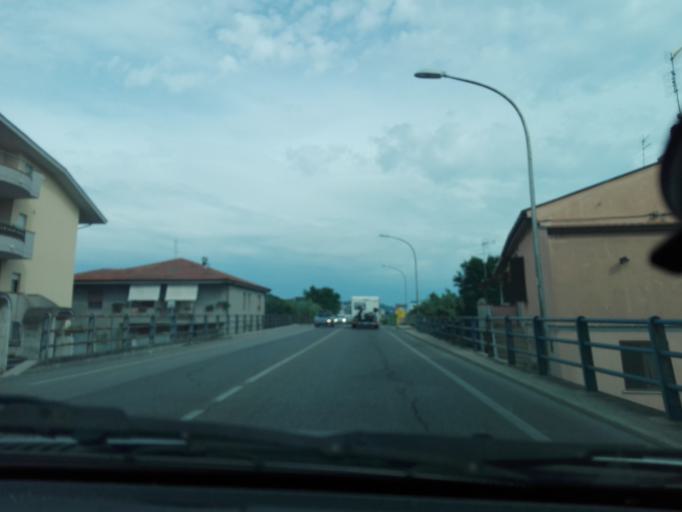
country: IT
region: Abruzzo
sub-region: Provincia di Pescara
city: San Martino Bassa
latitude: 42.5293
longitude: 14.1345
